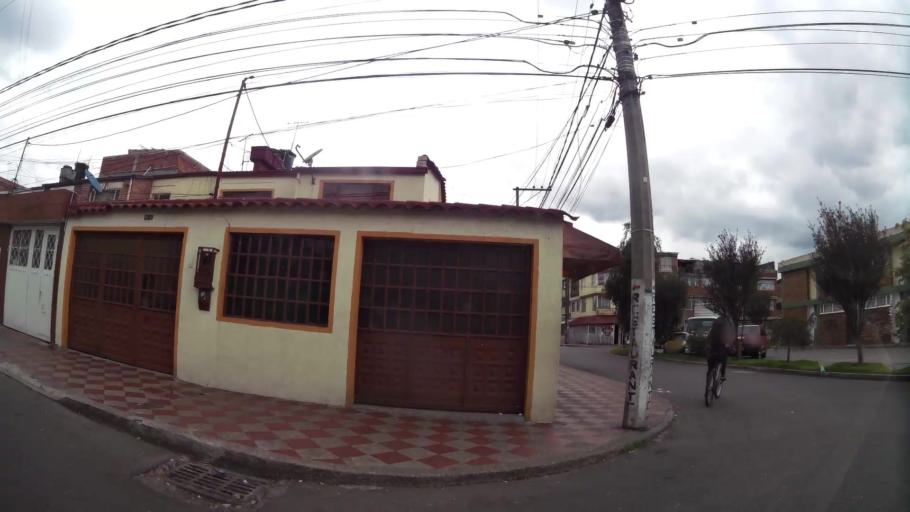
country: CO
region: Bogota D.C.
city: Bogota
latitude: 4.6183
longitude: -74.1152
